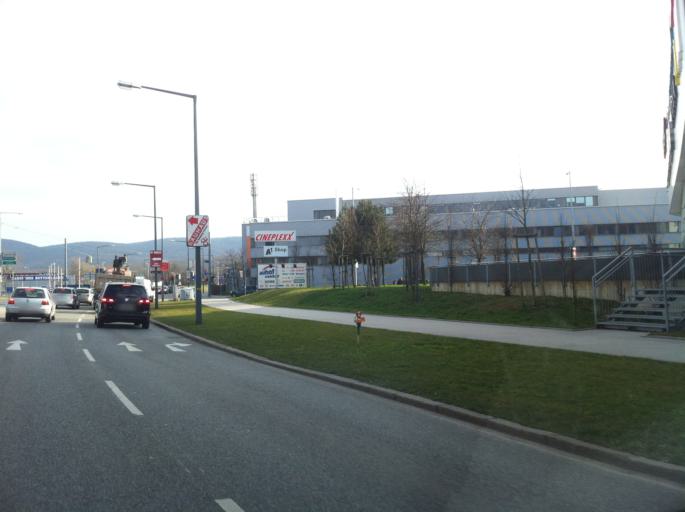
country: AT
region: Lower Austria
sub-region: Politischer Bezirk Wien-Umgebung
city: Purkersdorf
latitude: 48.2080
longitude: 16.2211
